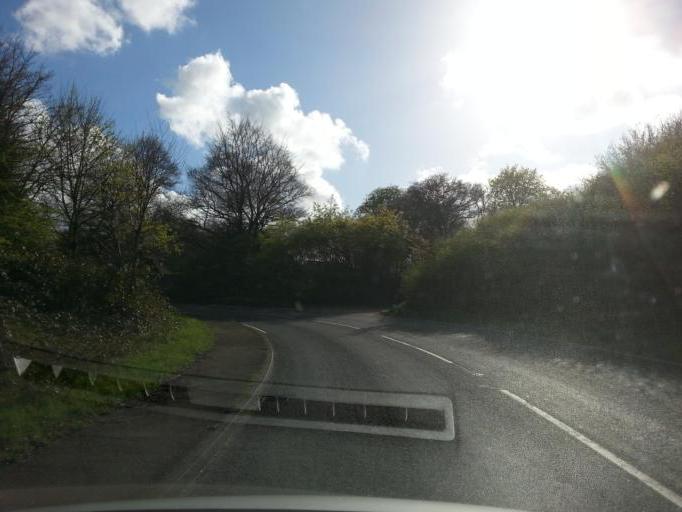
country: GB
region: England
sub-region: Surrey
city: Godalming
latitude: 51.2154
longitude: -0.6448
